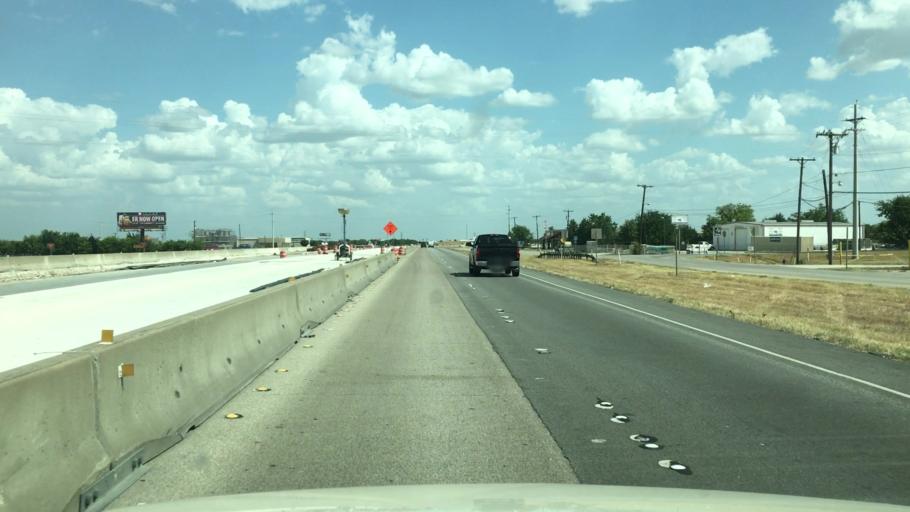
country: US
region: Texas
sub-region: Ellis County
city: Waxahachie
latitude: 32.3710
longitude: -96.8613
